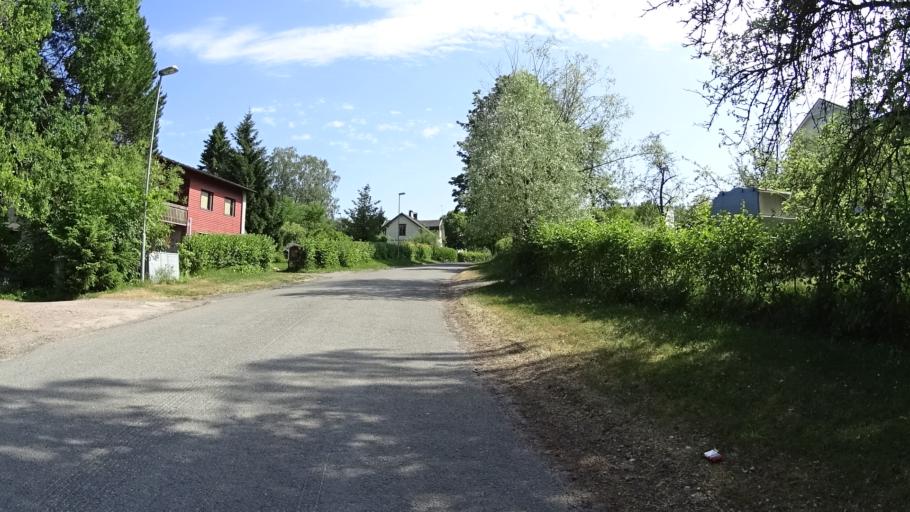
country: FI
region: Uusimaa
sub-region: Raaseporin
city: Karis
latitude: 60.0736
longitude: 23.6685
